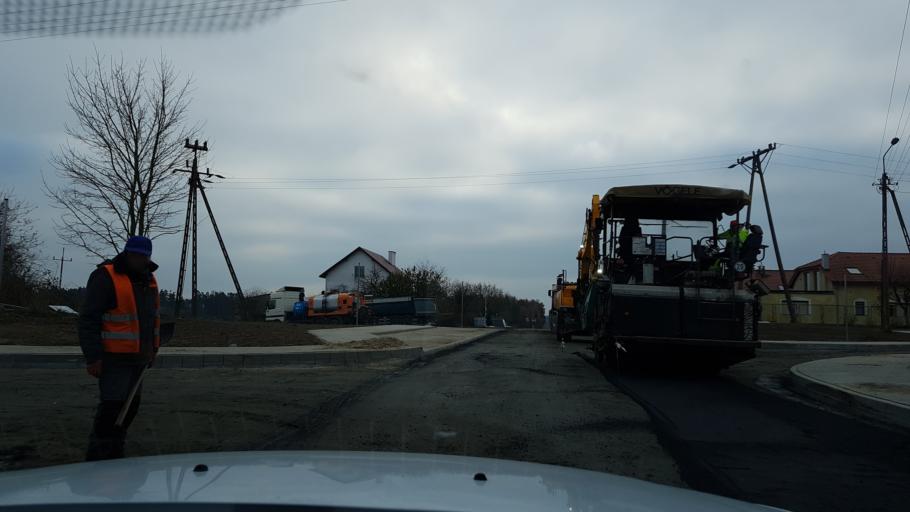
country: PL
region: West Pomeranian Voivodeship
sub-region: Powiat kolobrzeski
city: Grzybowo
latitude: 54.1173
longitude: 15.5241
